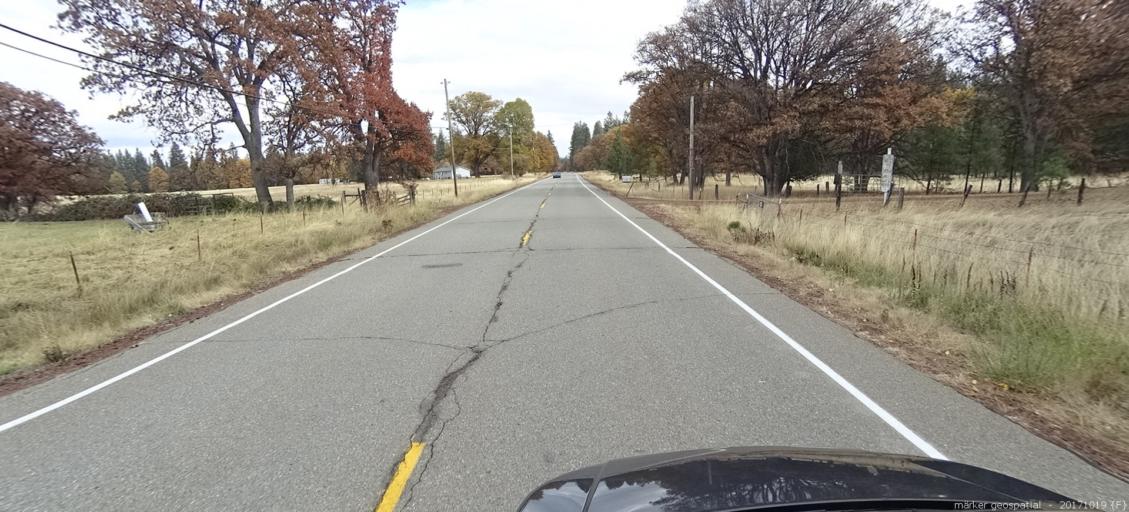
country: US
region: California
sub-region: Shasta County
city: Burney
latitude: 41.0945
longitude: -121.5438
